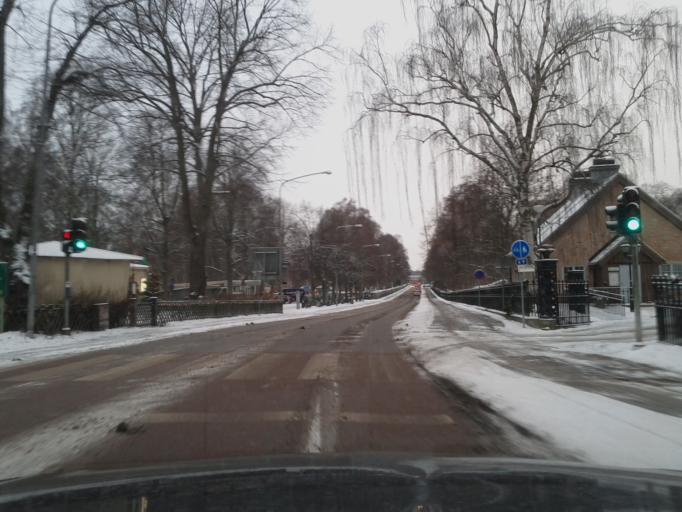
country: SE
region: Stockholm
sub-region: Norrtalje Kommun
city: Bergshamra
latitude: 59.3537
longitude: 18.0316
